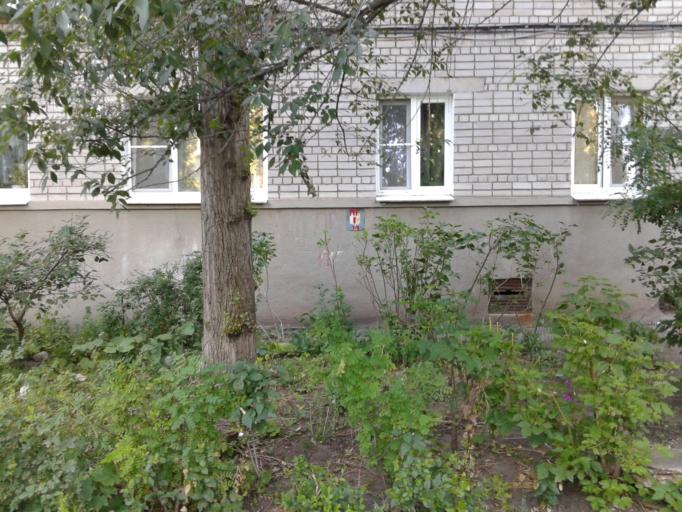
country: RU
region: Voronezj
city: Pridonskoy
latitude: 51.6578
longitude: 39.1160
